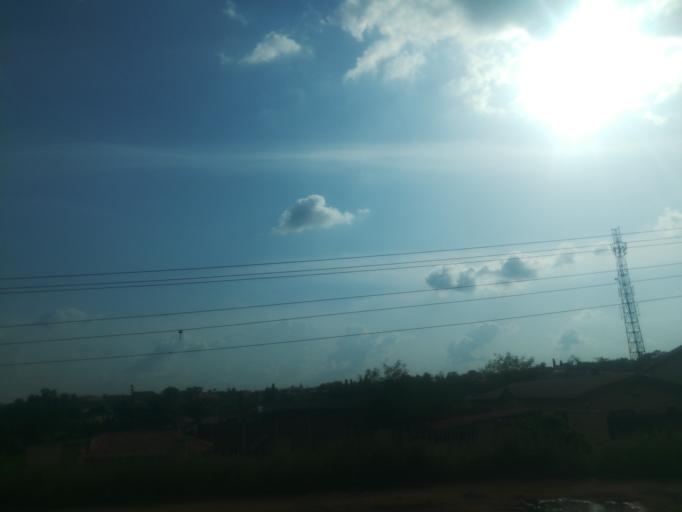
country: NG
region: Oyo
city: Ibadan
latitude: 7.3935
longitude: 3.8128
